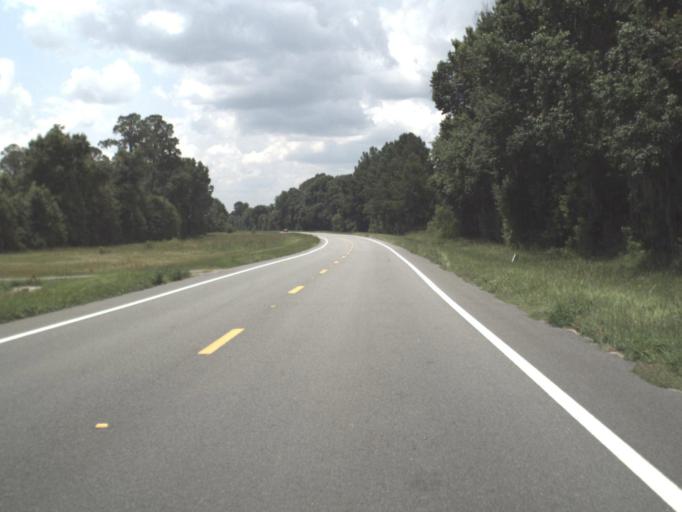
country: US
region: Florida
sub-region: Hamilton County
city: Jasper
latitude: 30.4778
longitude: -82.9143
